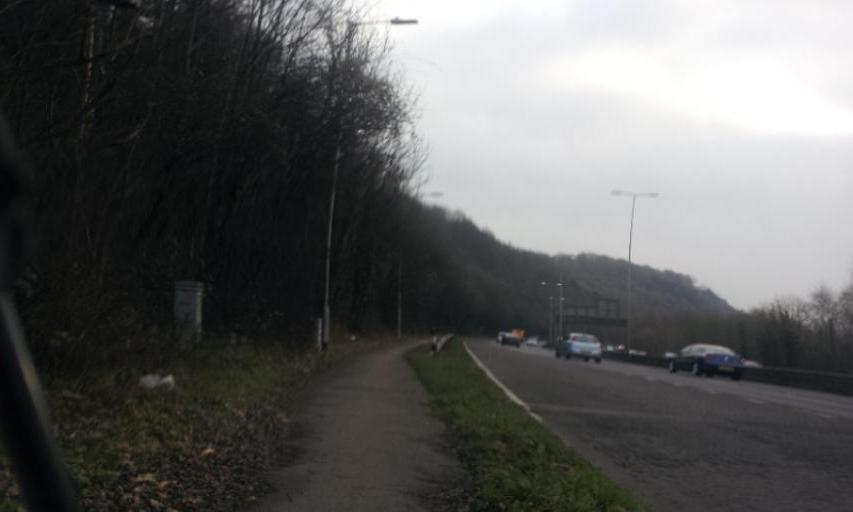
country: GB
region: England
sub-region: Kent
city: Aylesford
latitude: 51.3290
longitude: 0.5060
